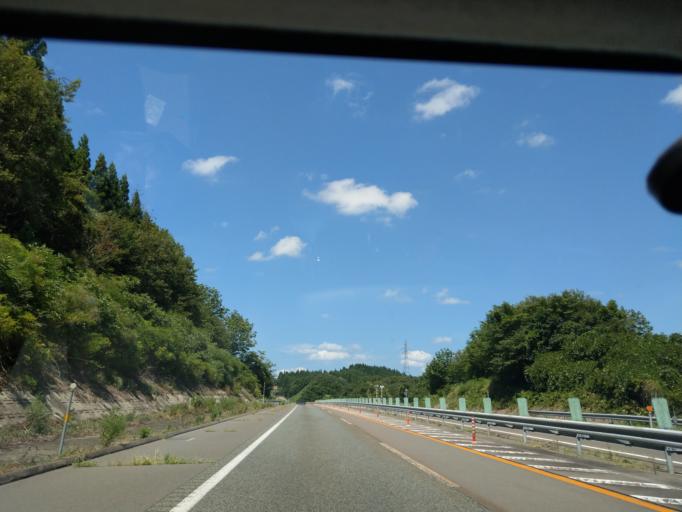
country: JP
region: Akita
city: Akita
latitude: 39.6671
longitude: 140.1884
